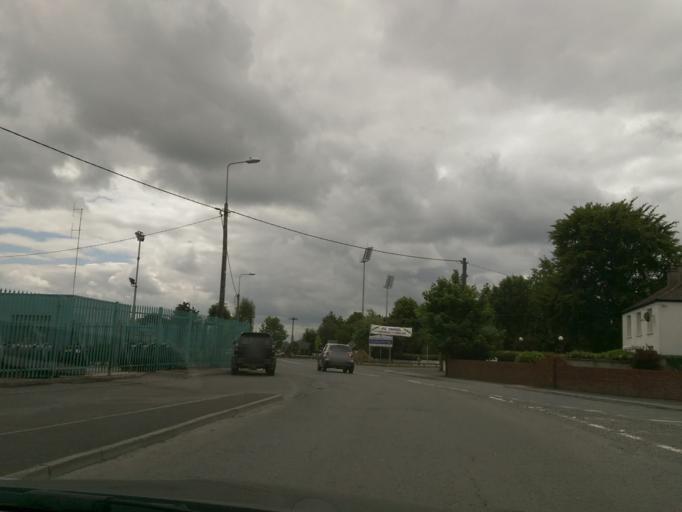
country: IE
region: Munster
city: Thurles
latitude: 52.6850
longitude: -7.8246
